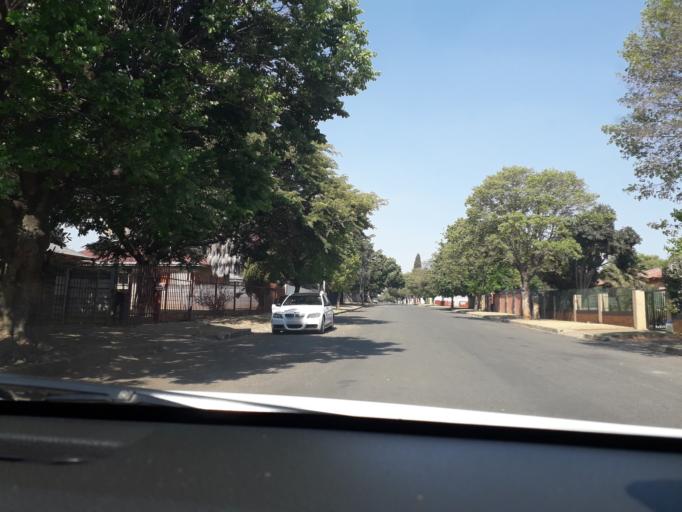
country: ZA
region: Gauteng
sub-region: City of Johannesburg Metropolitan Municipality
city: Modderfontein
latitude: -26.0982
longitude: 28.2297
